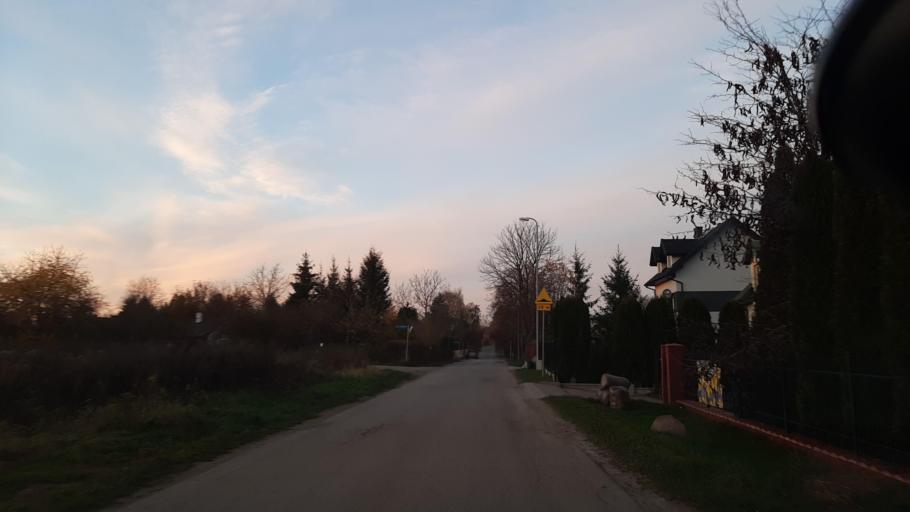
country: PL
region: Lublin Voivodeship
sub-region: Powiat lubelski
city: Jastkow
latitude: 51.2945
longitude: 22.5052
